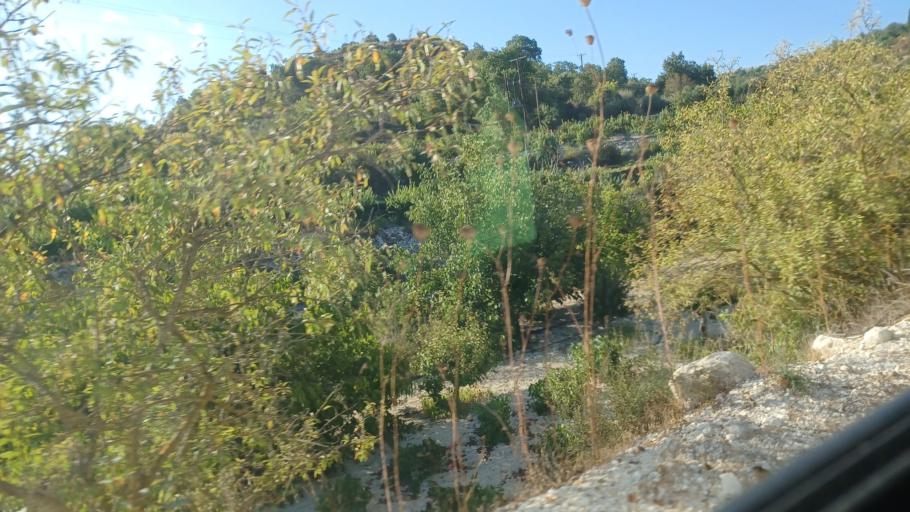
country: CY
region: Pafos
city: Mesogi
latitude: 34.8443
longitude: 32.4808
